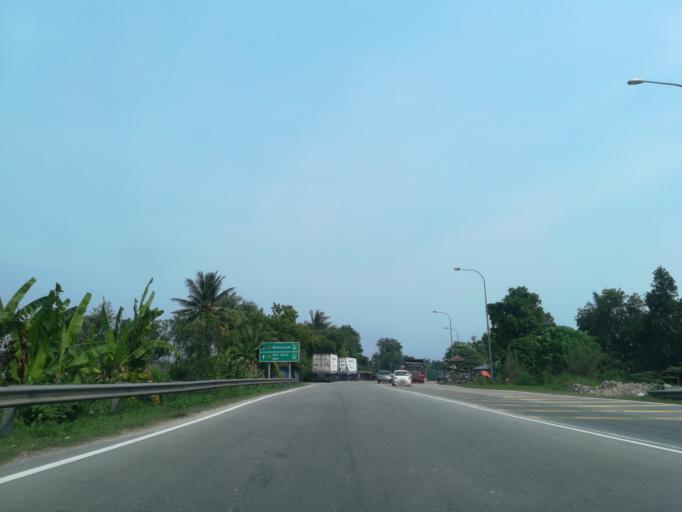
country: MY
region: Kedah
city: Kulim
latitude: 5.4305
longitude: 100.5533
